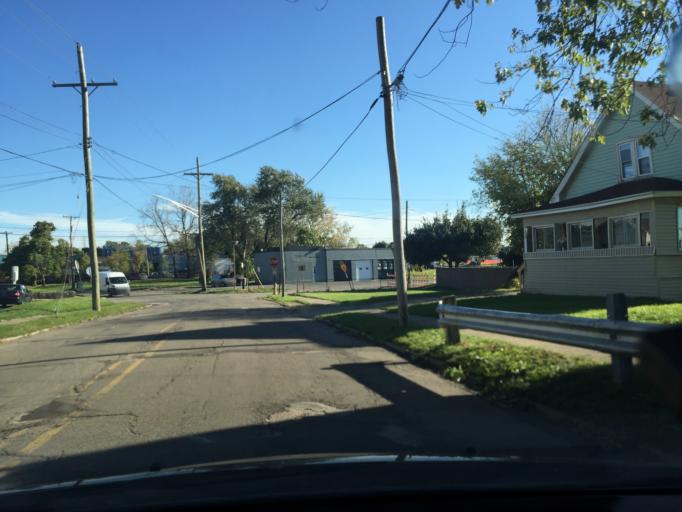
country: US
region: Michigan
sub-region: Oakland County
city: Pontiac
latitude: 42.6238
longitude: -83.2819
